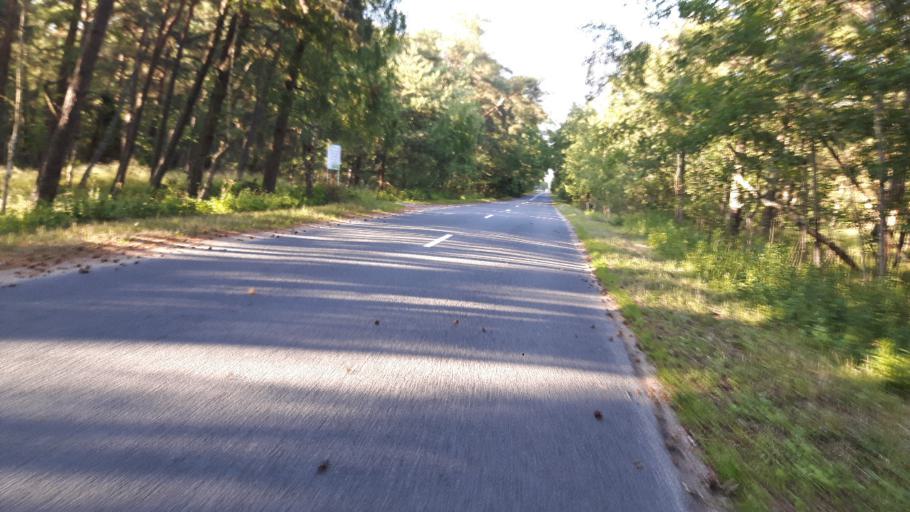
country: LT
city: Nida
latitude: 55.2599
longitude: 20.9386
